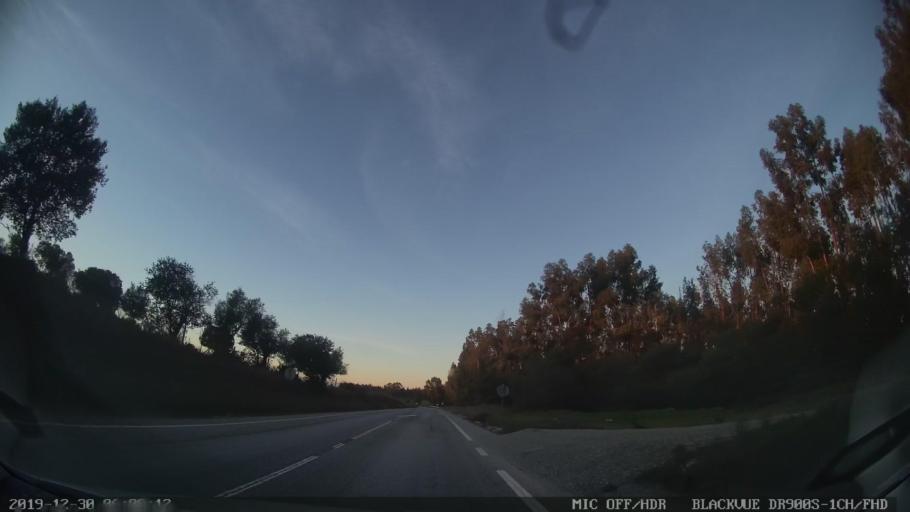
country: PT
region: Castelo Branco
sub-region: Idanha-A-Nova
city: Idanha-a-Nova
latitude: 40.0502
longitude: -7.2445
